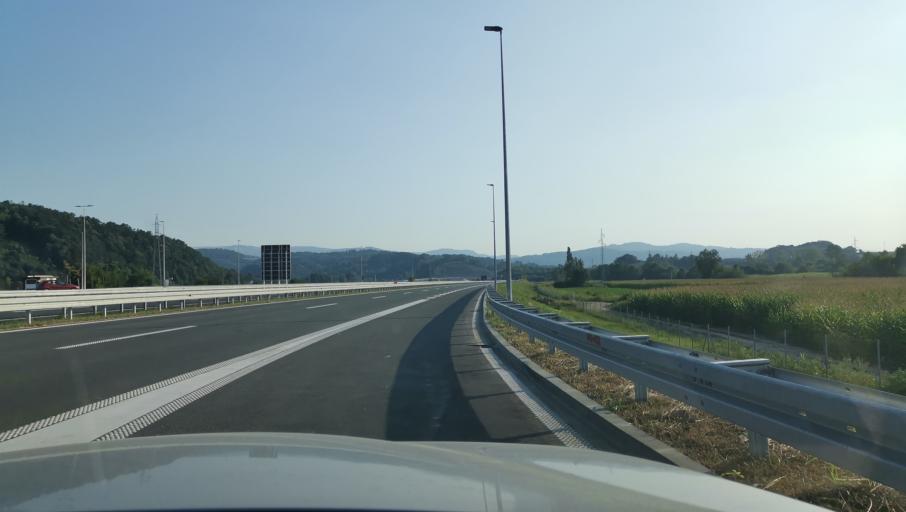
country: RS
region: Central Serbia
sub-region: Kolubarski Okrug
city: Ljig
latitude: 44.2421
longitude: 20.2628
